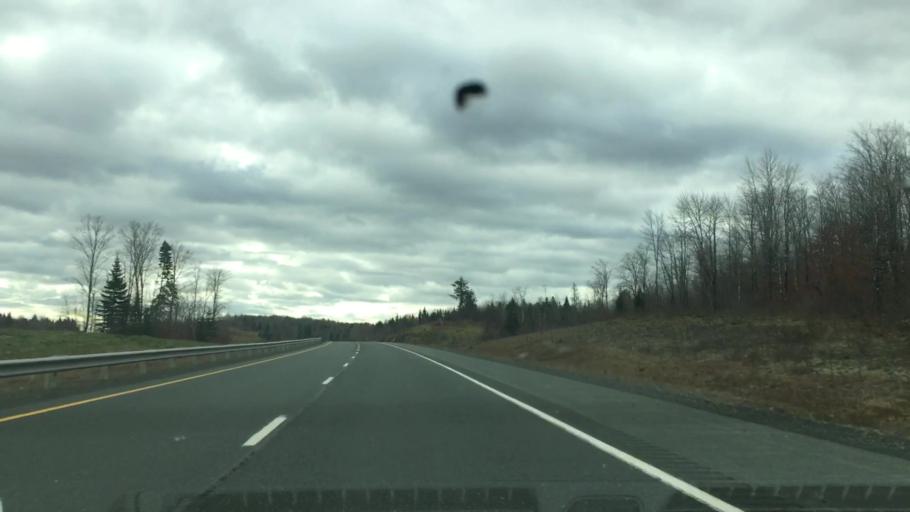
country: US
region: Maine
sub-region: Aroostook County
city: Fort Fairfield
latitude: 46.6442
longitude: -67.7441
